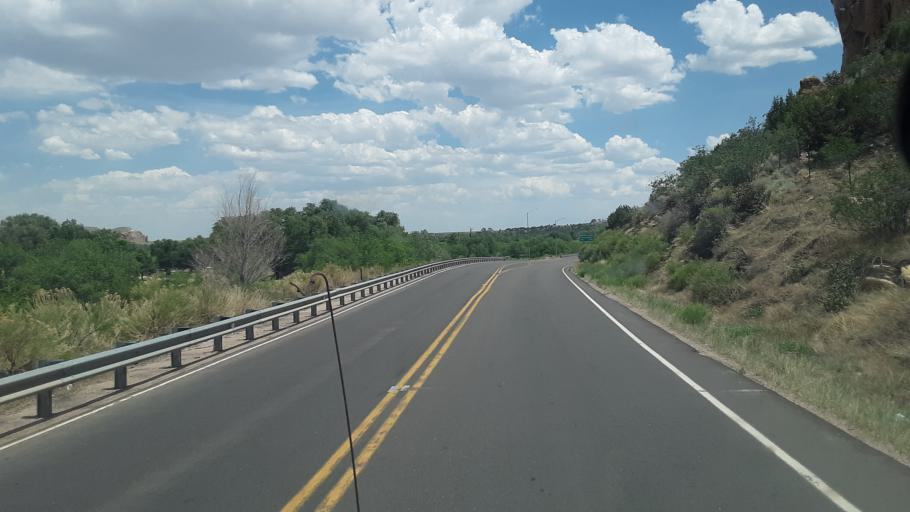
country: US
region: Colorado
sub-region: Fremont County
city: Lincoln Park
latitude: 38.4144
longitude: -105.1791
